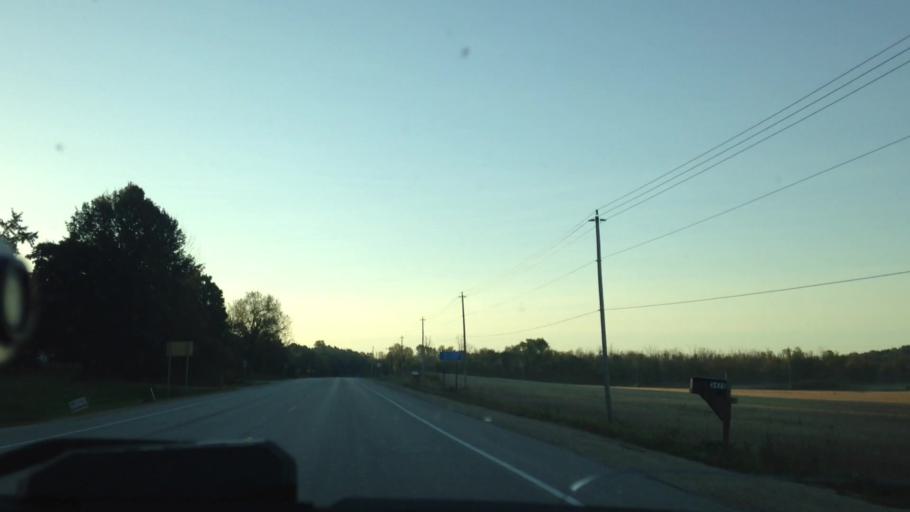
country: US
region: Wisconsin
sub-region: Washington County
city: Newburg
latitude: 43.4277
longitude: -88.0387
